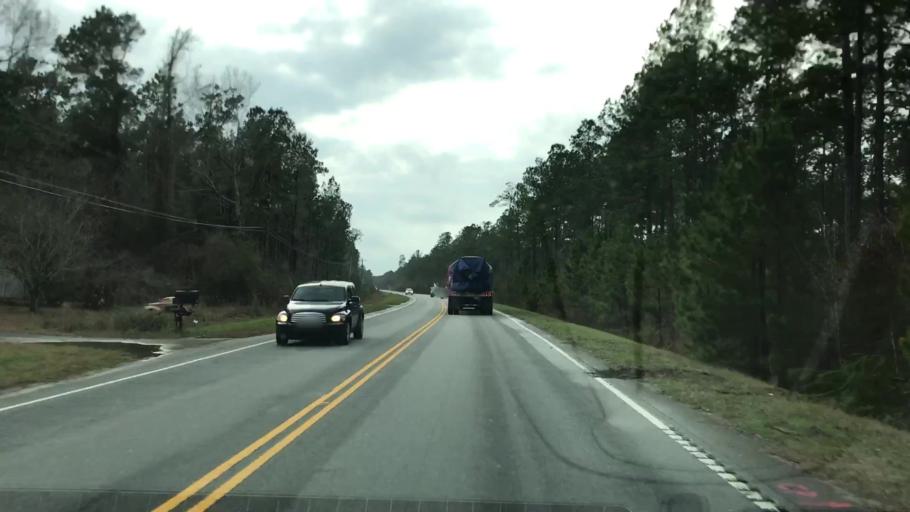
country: US
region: South Carolina
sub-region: Berkeley County
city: Bonneau Beach
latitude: 33.2645
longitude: -79.9217
